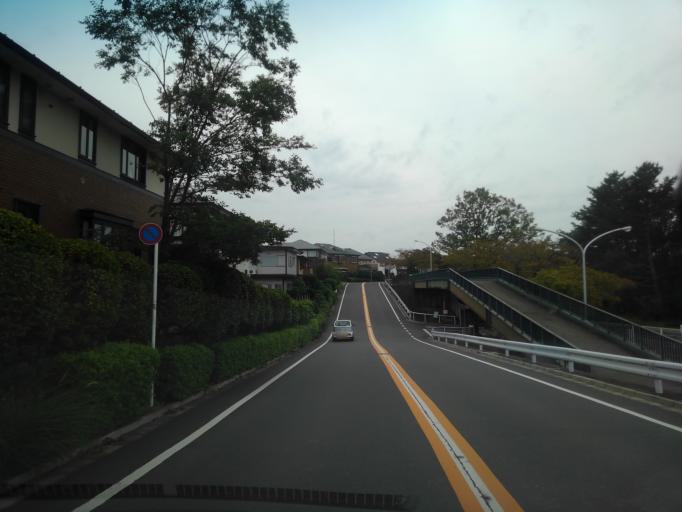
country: JP
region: Tokyo
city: Higashimurayama-shi
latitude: 35.7673
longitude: 139.4458
